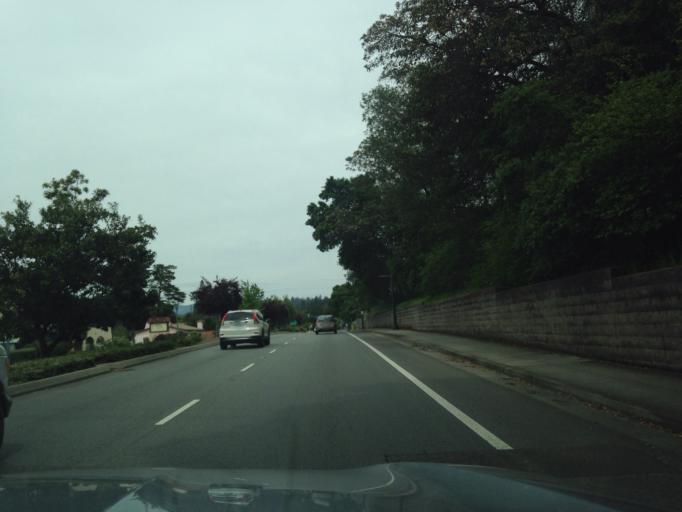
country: US
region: California
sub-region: Santa Cruz County
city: Scotts Valley
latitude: 37.0455
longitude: -122.0211
